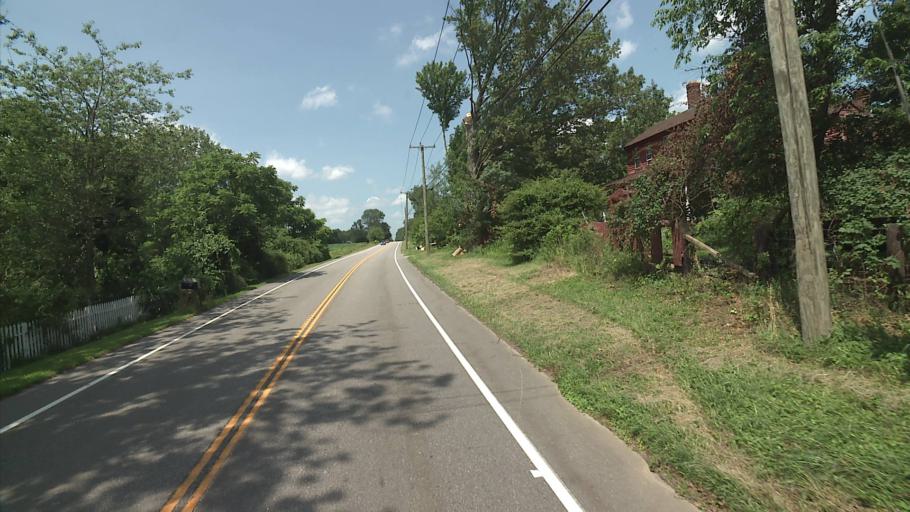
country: US
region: Connecticut
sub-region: Tolland County
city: Coventry Lake
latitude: 41.8052
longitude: -72.3947
